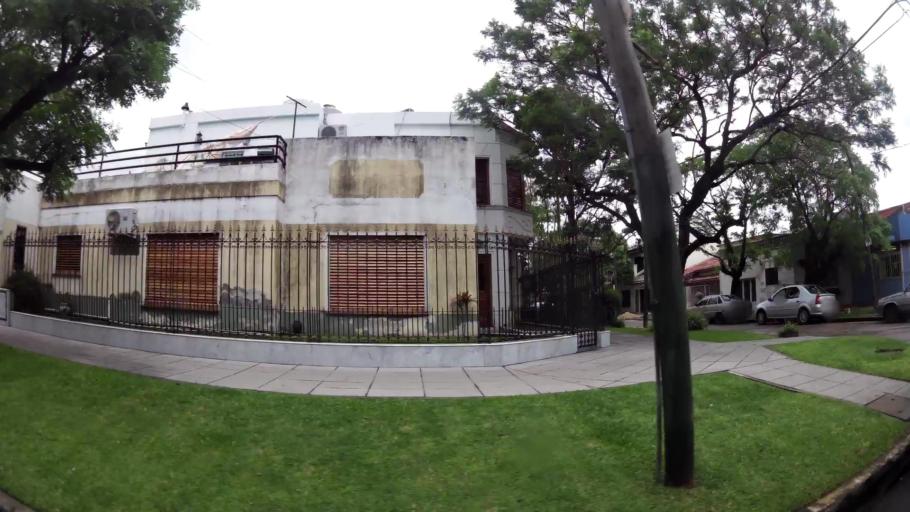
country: AR
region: Buenos Aires
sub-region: Partido de Lomas de Zamora
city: Lomas de Zamora
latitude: -34.7495
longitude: -58.3847
